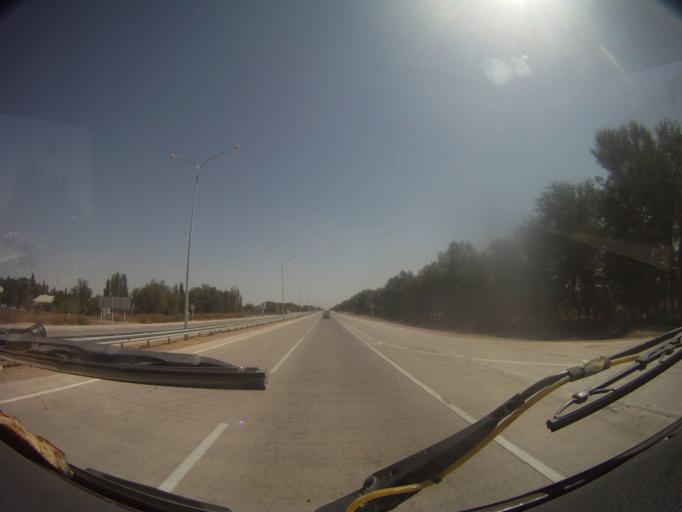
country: KZ
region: Ongtustik Qazaqstan
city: Temirlanovka
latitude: 42.9000
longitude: 68.9972
